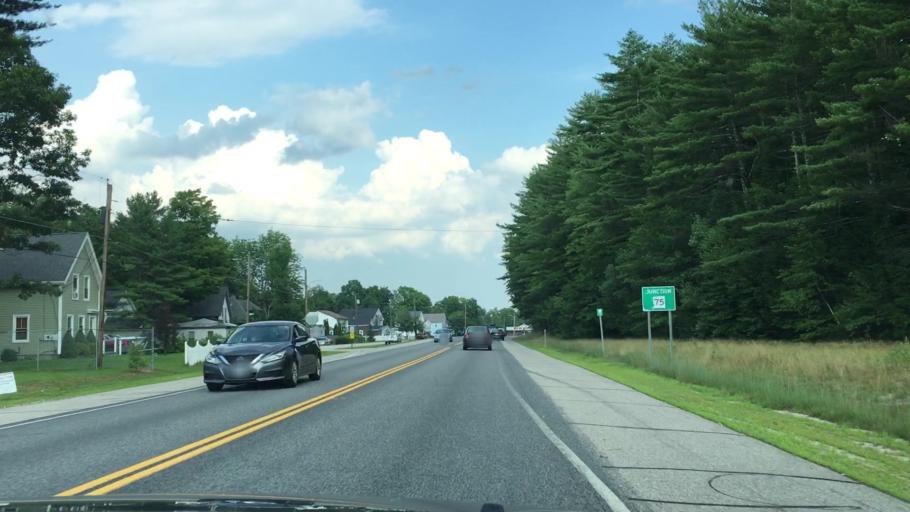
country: US
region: New Hampshire
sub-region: Strafford County
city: Farmington
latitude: 43.3860
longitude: -71.0792
